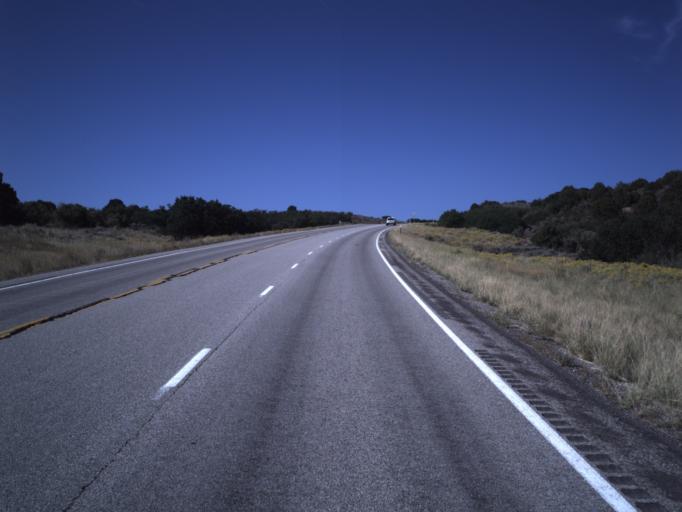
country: US
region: Utah
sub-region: San Juan County
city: Monticello
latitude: 37.7736
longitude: -109.3582
